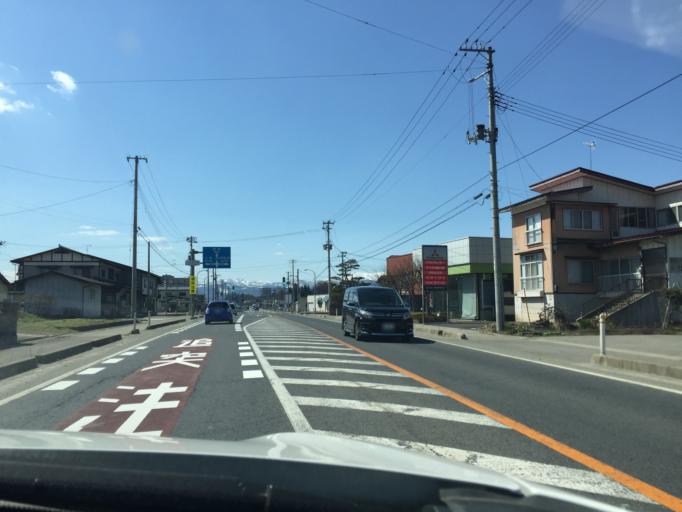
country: JP
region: Yamagata
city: Nagai
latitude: 38.0505
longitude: 140.0669
